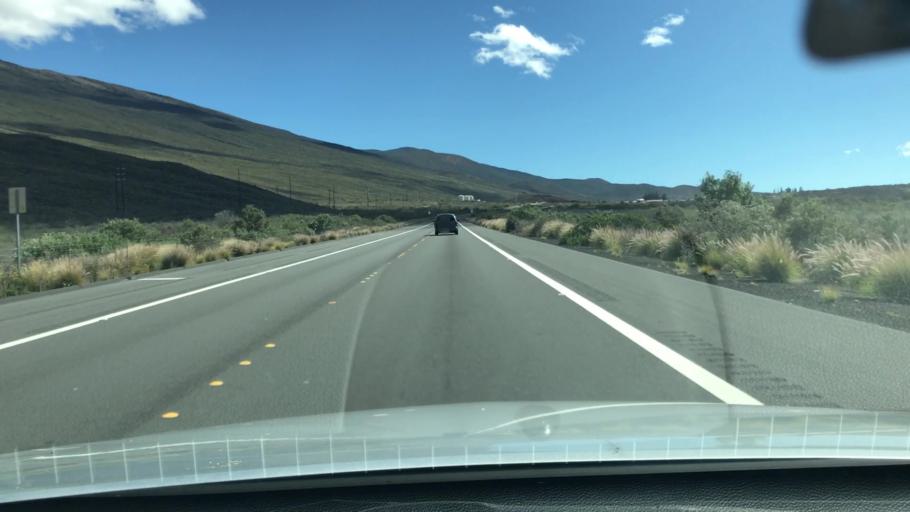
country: US
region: Hawaii
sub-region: Hawaii County
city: Waimea
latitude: 19.7639
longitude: -155.5558
